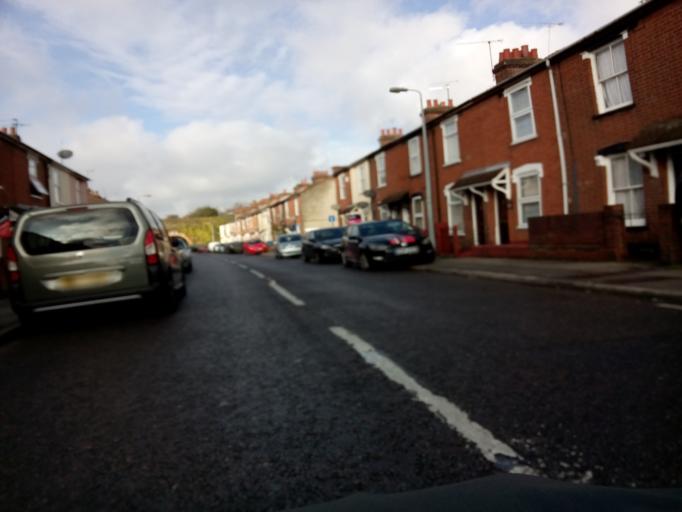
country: GB
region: England
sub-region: Suffolk
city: Ipswich
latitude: 52.0682
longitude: 1.1312
